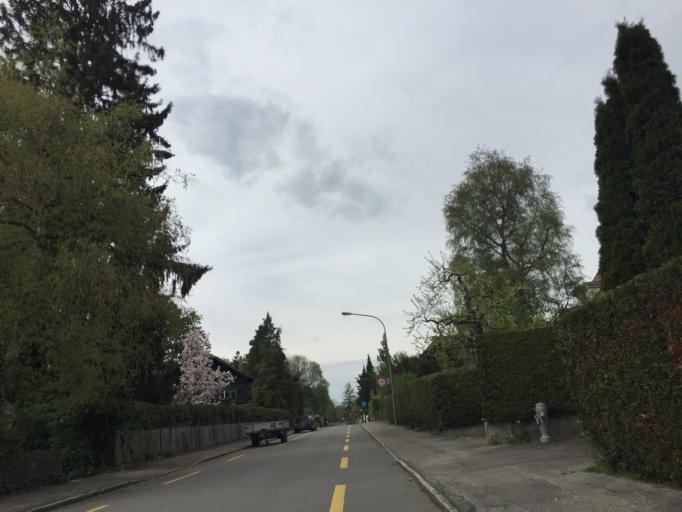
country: CH
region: Bern
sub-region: Bern-Mittelland District
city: Muri
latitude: 46.9327
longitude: 7.4796
